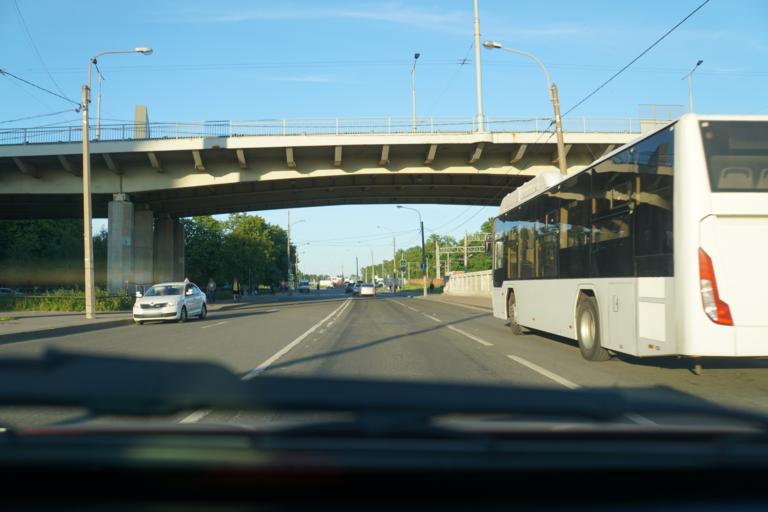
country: RU
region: St.-Petersburg
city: Avtovo
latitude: 59.8645
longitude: 30.2740
